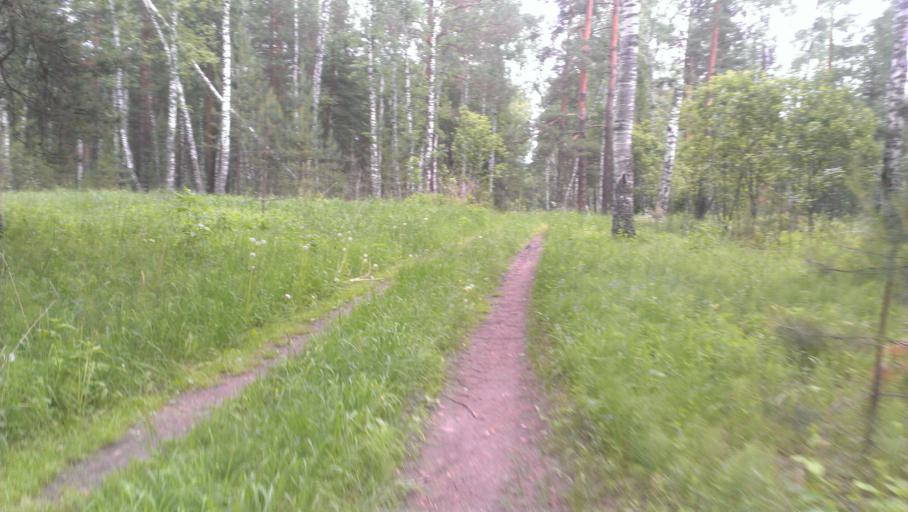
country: RU
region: Altai Krai
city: Sannikovo
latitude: 53.3457
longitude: 84.0420
